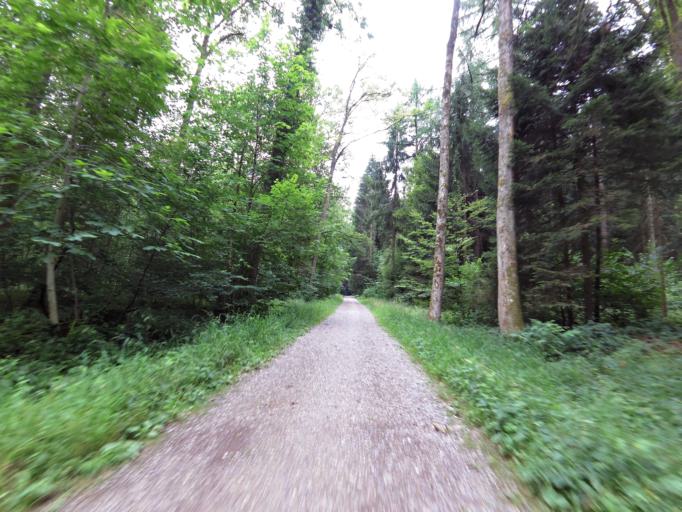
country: CH
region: Zurich
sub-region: Bezirk Zuerich
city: Zuerich (Kreis 10) / Ruetihof
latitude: 47.4140
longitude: 8.4888
